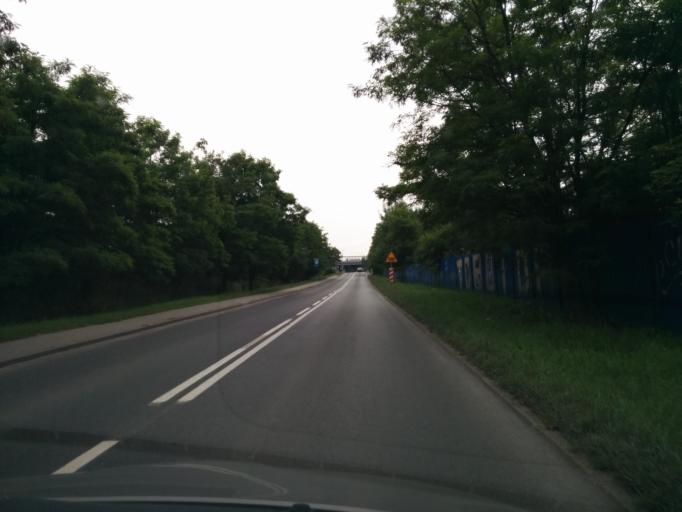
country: PL
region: Silesian Voivodeship
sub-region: Ruda Slaska
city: Ruda Slaska
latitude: 50.2608
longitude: 18.8388
